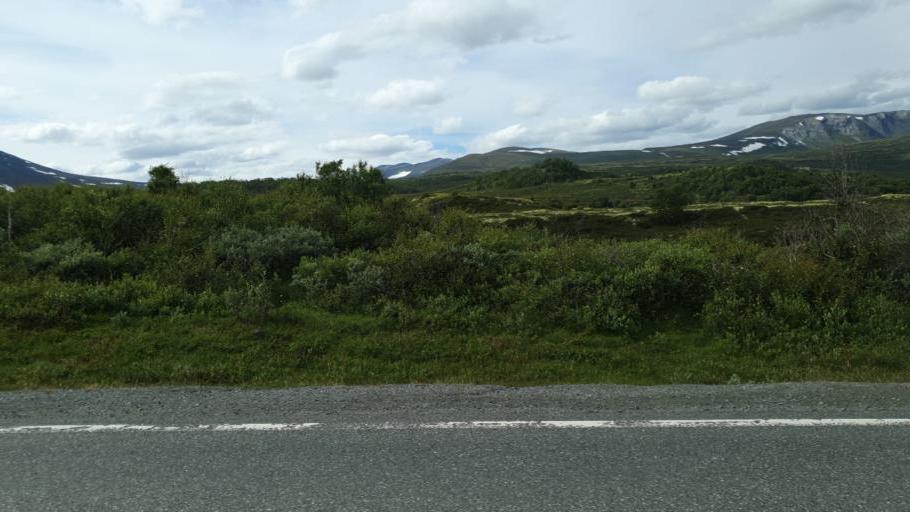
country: NO
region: Sor-Trondelag
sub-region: Oppdal
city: Oppdal
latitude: 62.2796
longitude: 9.5980
